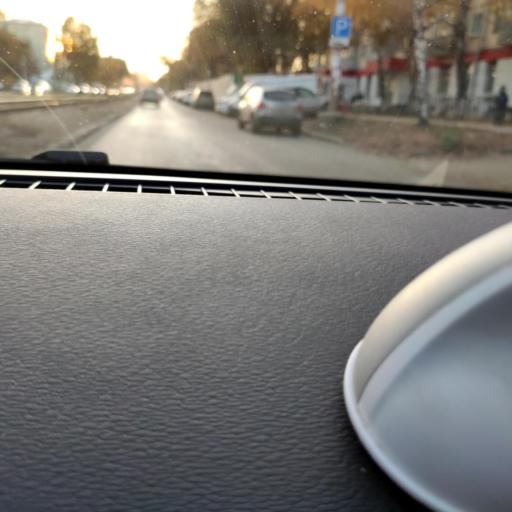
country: RU
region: Samara
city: Samara
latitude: 53.2205
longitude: 50.2290
